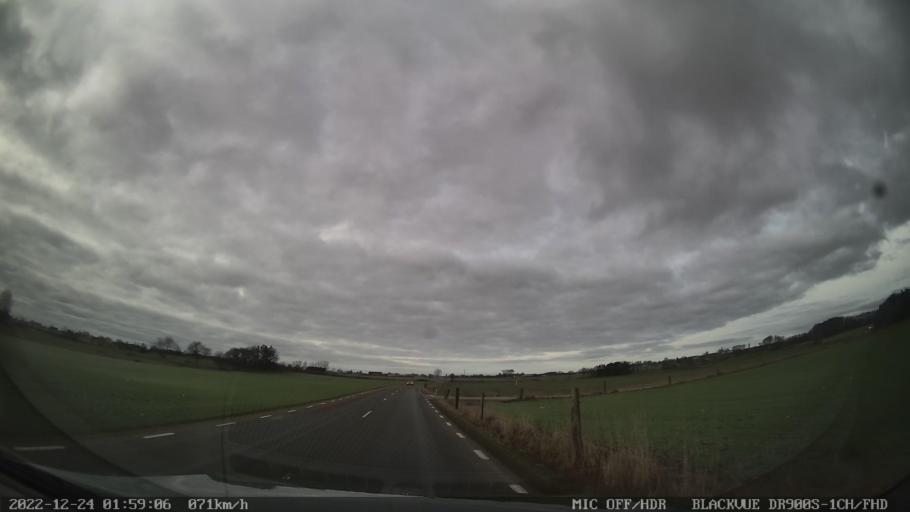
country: SE
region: Skane
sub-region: Tomelilla Kommun
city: Tomelilla
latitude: 55.6065
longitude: 14.0212
